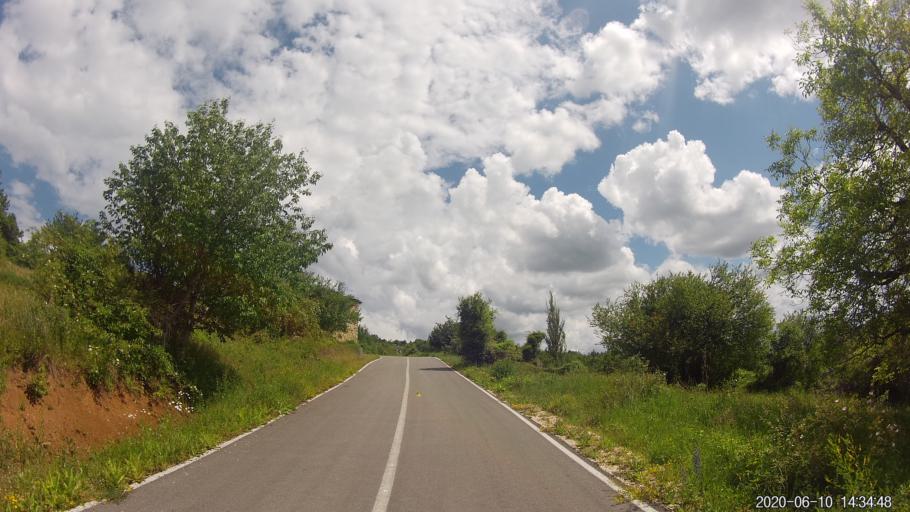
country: XK
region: Prizren
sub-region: Komuna e Therandes
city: Budakovo
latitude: 42.4146
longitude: 20.9322
